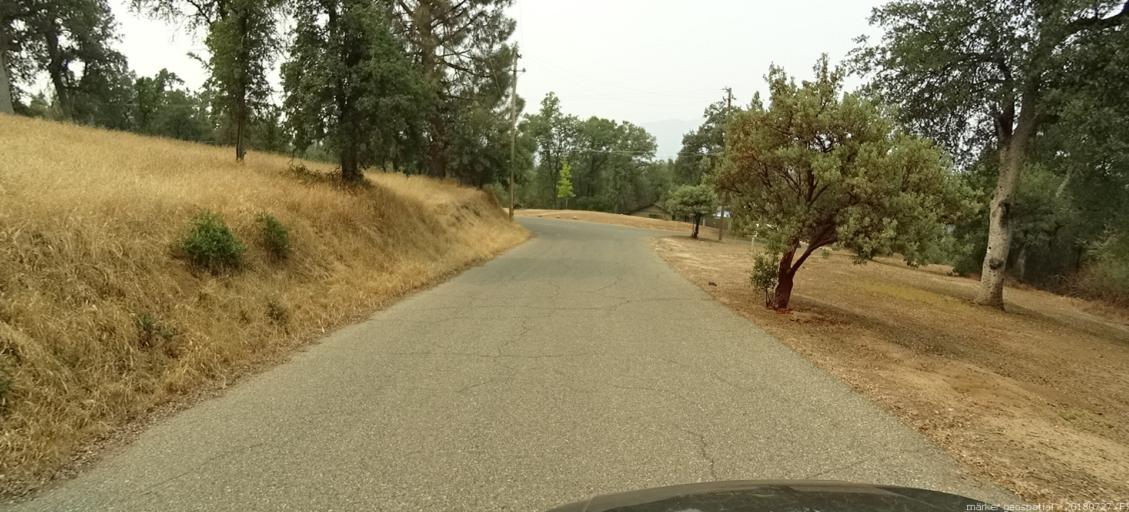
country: US
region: California
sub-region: Madera County
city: Oakhurst
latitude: 37.3412
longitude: -119.6343
